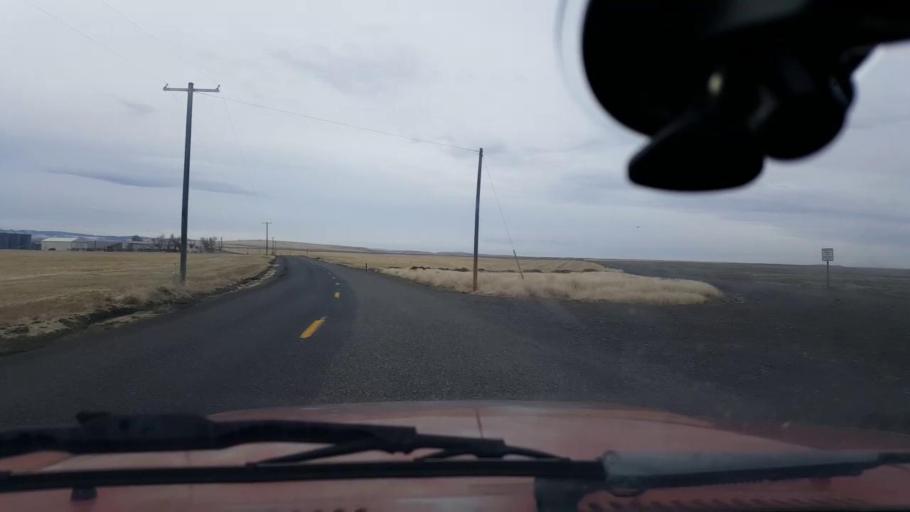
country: US
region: Washington
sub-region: Asotin County
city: Clarkston Heights-Vineland
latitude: 46.3747
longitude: -117.1646
